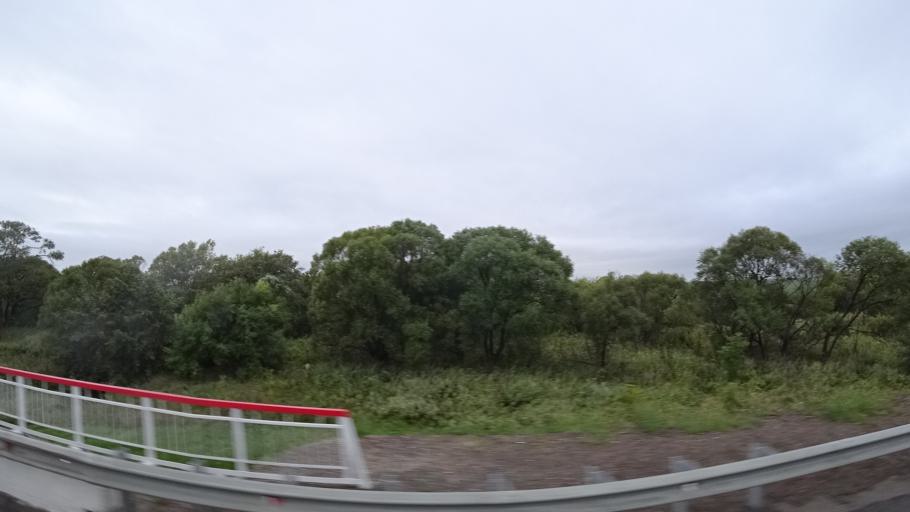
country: RU
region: Primorskiy
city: Chernigovka
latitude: 44.2889
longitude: 132.5045
